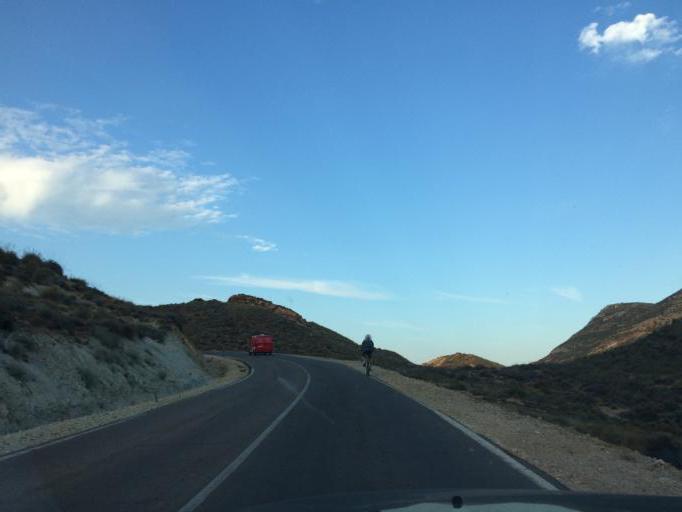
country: ES
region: Andalusia
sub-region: Provincia de Almeria
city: San Jose
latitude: 36.8660
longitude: -2.0286
